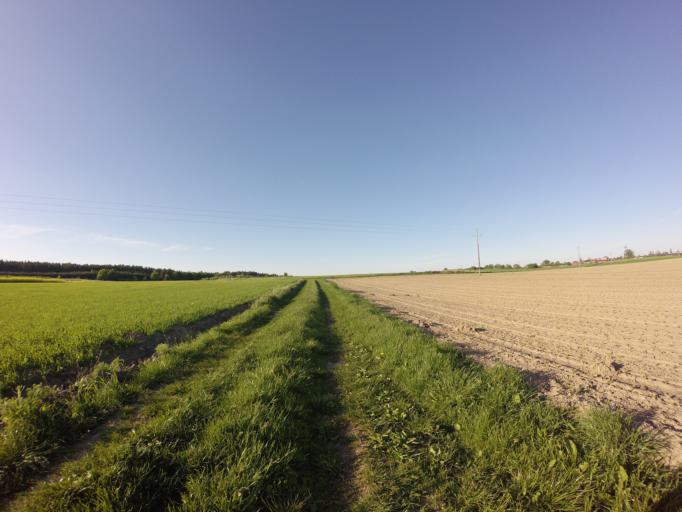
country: PL
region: West Pomeranian Voivodeship
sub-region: Powiat choszczenski
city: Choszczno
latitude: 53.1626
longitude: 15.3858
